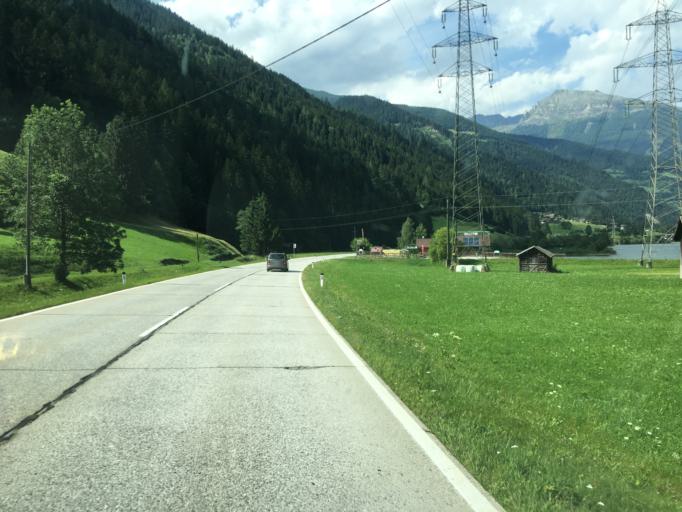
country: AT
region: Carinthia
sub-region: Politischer Bezirk Spittal an der Drau
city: Stall
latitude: 46.9067
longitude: 13.0666
